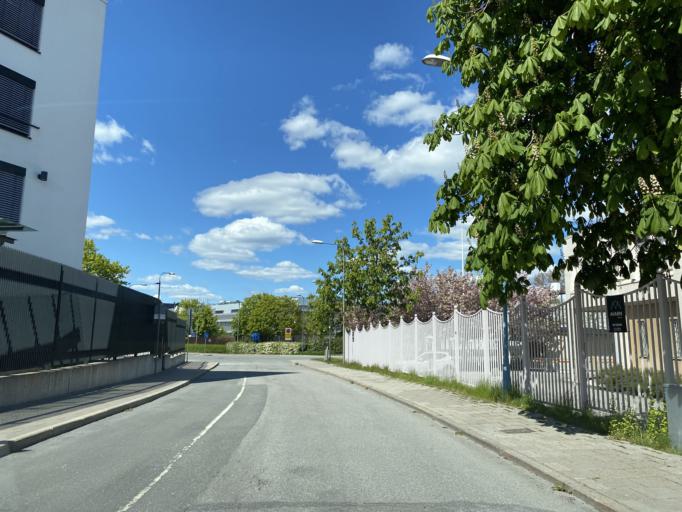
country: SE
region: Stockholm
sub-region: Stockholms Kommun
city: OEstermalm
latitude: 59.3345
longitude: 18.1067
